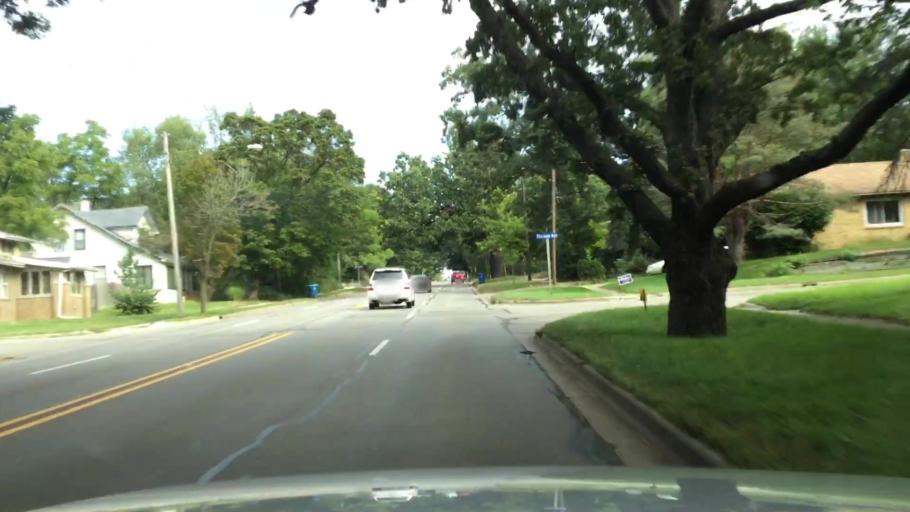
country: US
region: Michigan
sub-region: Kalamazoo County
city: Kalamazoo
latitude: 42.2631
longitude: -85.5896
